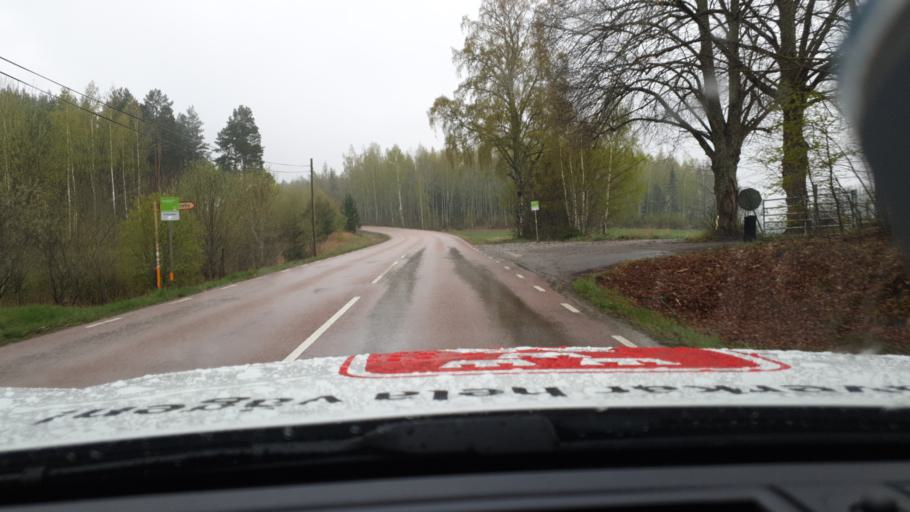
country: SE
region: Soedermanland
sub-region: Strangnas Kommun
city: Stallarholmen
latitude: 59.3527
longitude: 17.2166
